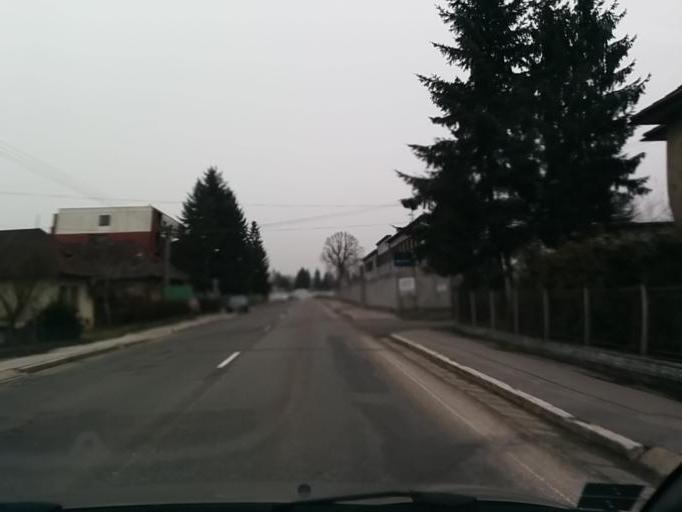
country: SK
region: Banskobystricky
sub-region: Okres Banska Bystrica
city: Zvolen
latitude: 48.6191
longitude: 19.1372
